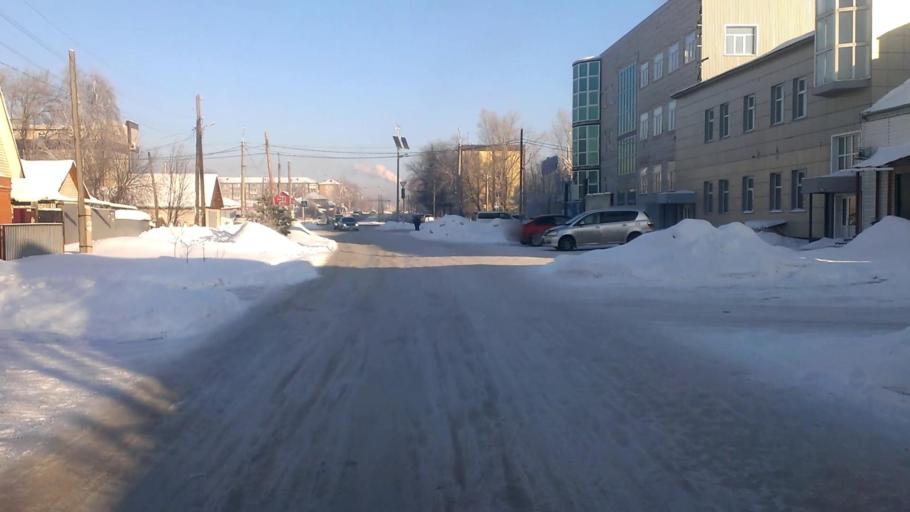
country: RU
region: Altai Krai
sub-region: Gorod Barnaulskiy
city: Barnaul
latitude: 53.3483
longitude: 83.7273
